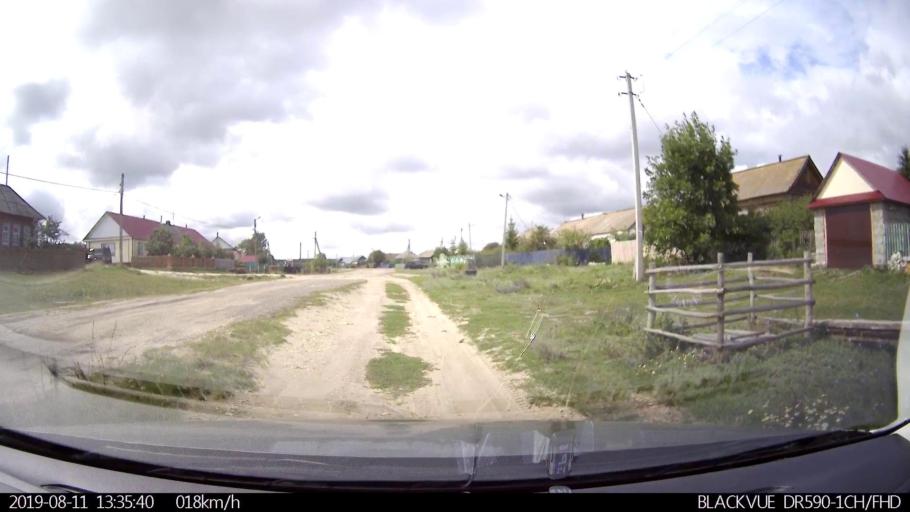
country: RU
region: Ulyanovsk
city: Ignatovka
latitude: 53.8599
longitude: 47.5896
